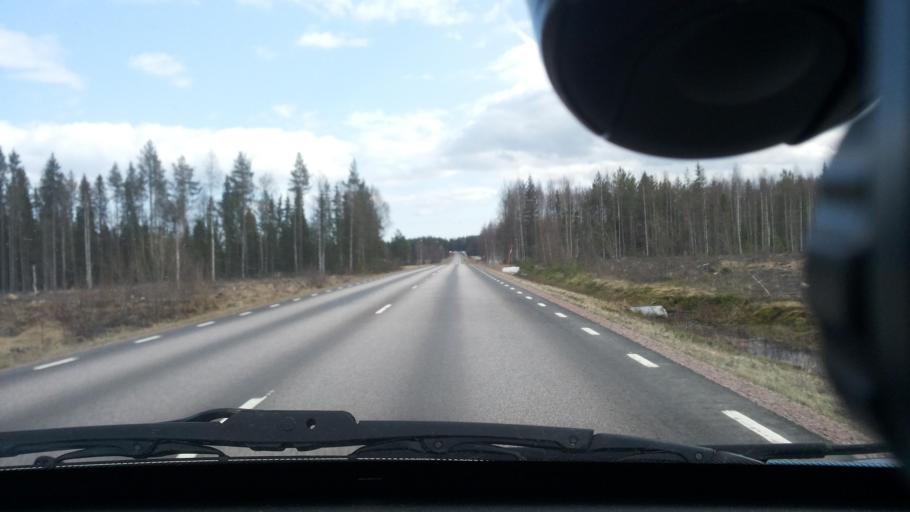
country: SE
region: Norrbotten
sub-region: Lulea Kommun
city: Sodra Sunderbyn
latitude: 65.6154
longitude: 21.9494
